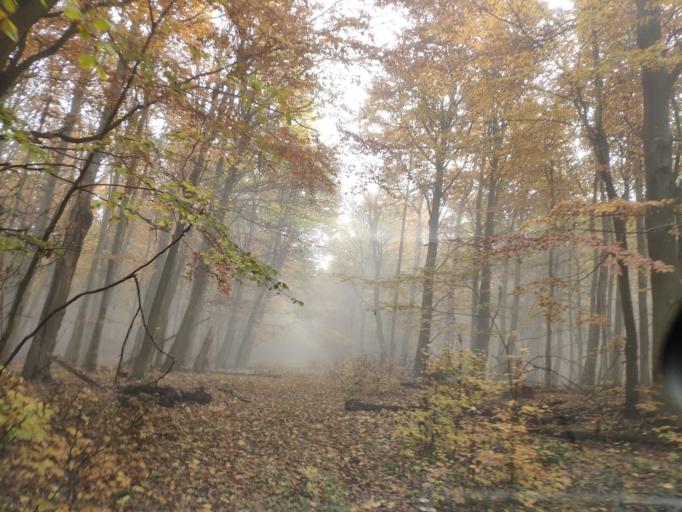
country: SK
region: Kosicky
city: Medzev
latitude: 48.7365
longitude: 21.0010
